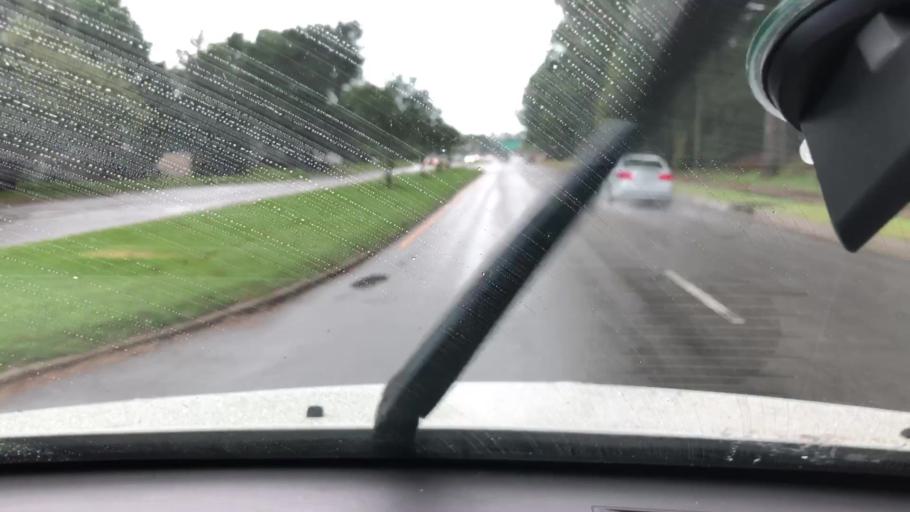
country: US
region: Virginia
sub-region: City of Chesapeake
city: Chesapeake
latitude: 36.8262
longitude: -76.1454
